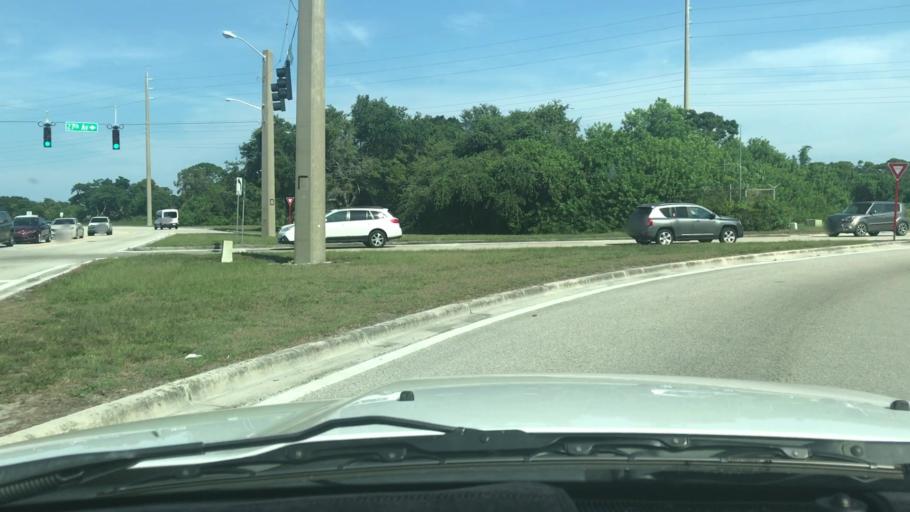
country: US
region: Florida
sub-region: Indian River County
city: Vero Beach
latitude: 27.6464
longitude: -80.4138
